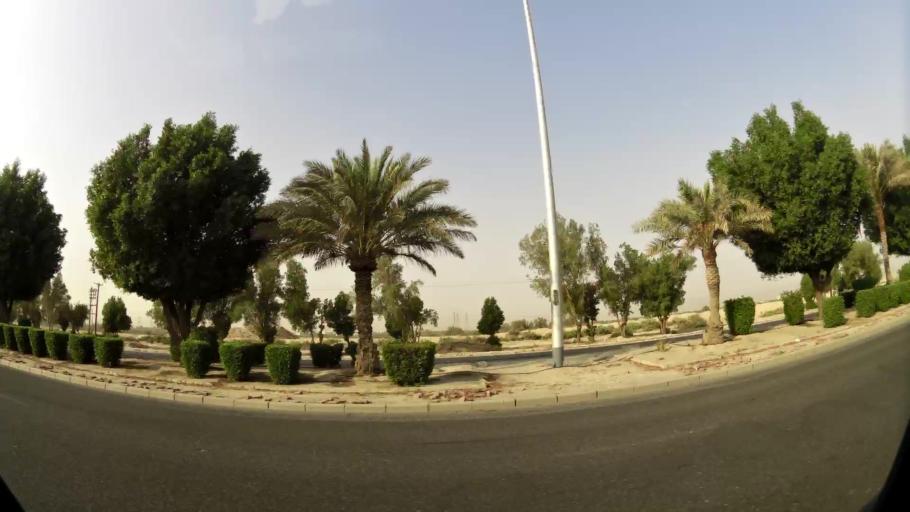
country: KW
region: Al Asimah
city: Ar Rabiyah
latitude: 29.3178
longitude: 47.8050
